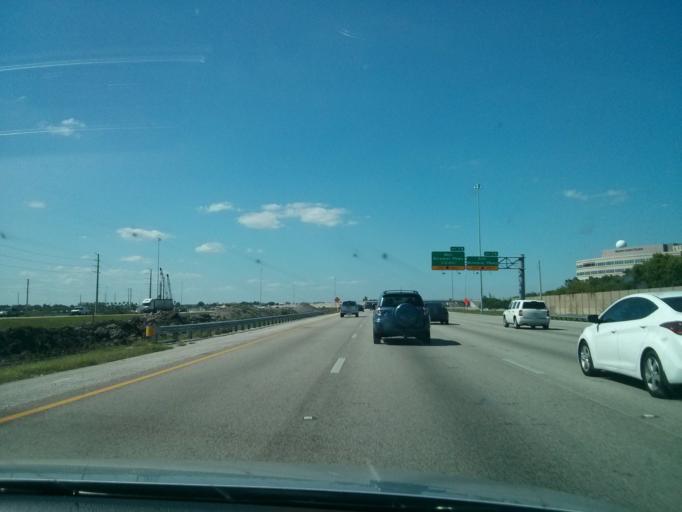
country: US
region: Florida
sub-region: Miami-Dade County
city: Palm Springs North
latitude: 25.9706
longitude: -80.3520
